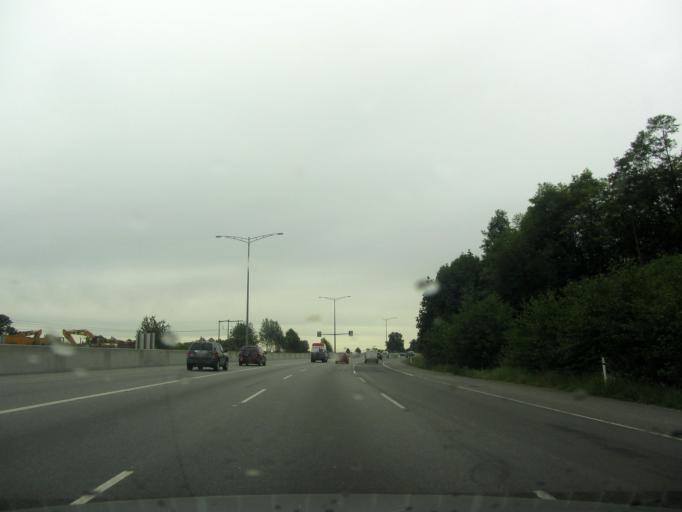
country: CA
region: British Columbia
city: Burnaby
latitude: 49.2574
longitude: -123.0159
